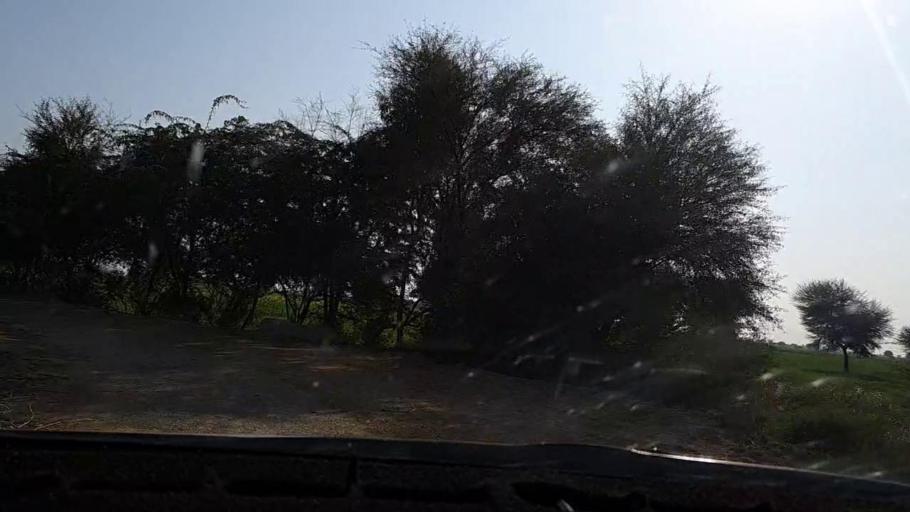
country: PK
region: Sindh
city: Tando Mittha Khan
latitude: 25.8257
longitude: 69.2799
